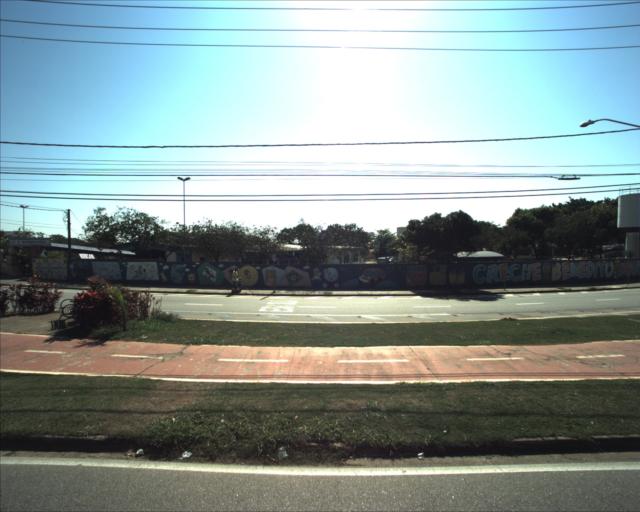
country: BR
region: Sao Paulo
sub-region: Sorocaba
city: Sorocaba
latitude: -23.5054
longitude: -47.5139
